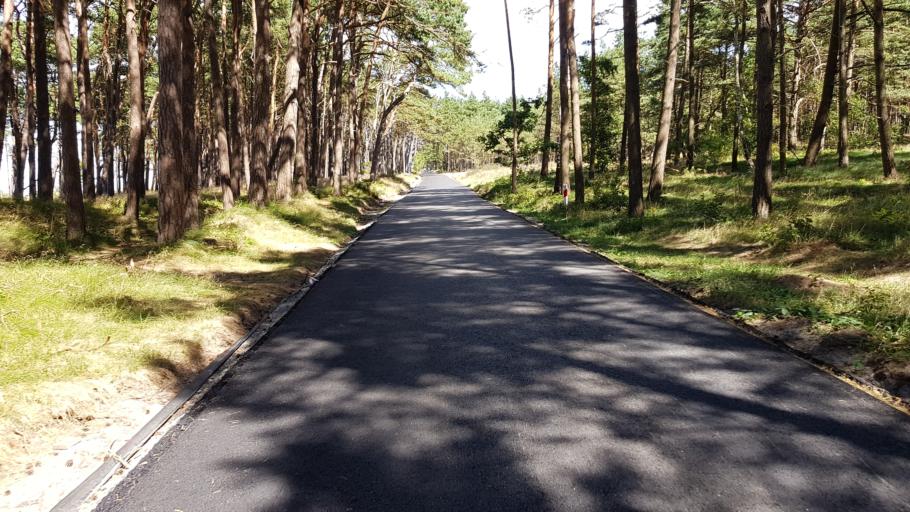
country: PL
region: West Pomeranian Voivodeship
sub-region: Powiat slawienski
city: Darlowo
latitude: 54.4977
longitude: 16.4507
